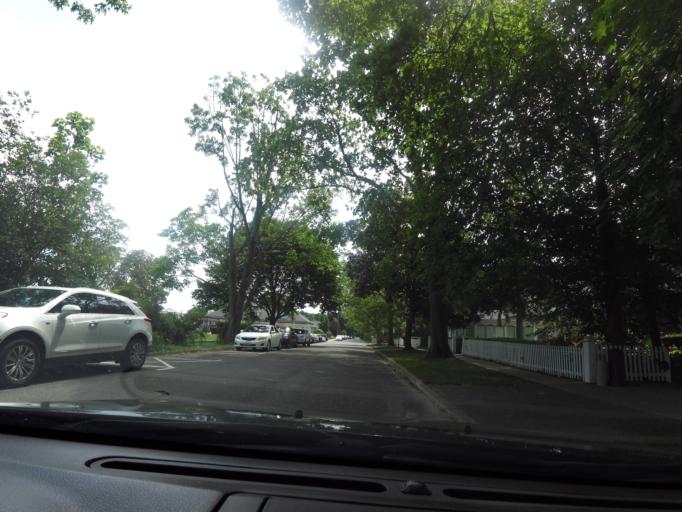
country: US
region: New York
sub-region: Niagara County
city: Youngstown
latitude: 43.2598
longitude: -79.0743
